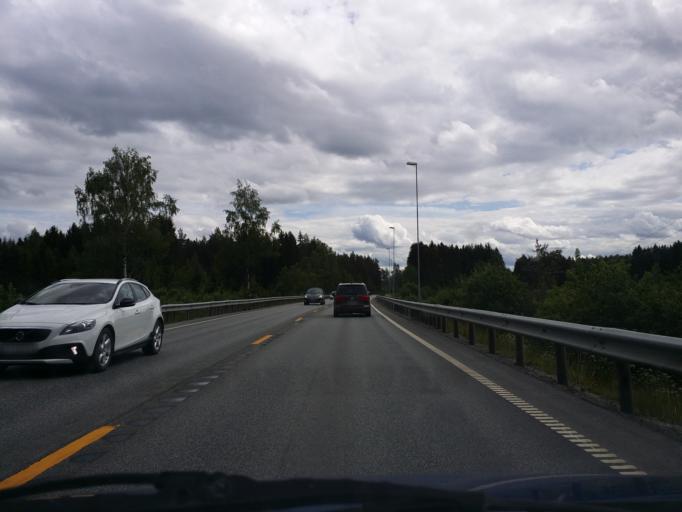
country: NO
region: Hedmark
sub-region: Stange
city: Stange
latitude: 60.7432
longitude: 11.2058
